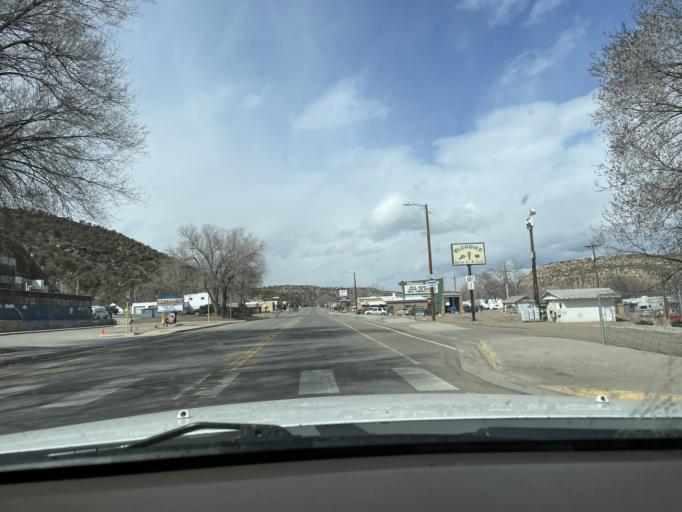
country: US
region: Colorado
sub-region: Dolores County
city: Dove Creek
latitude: 38.2171
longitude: -108.5687
